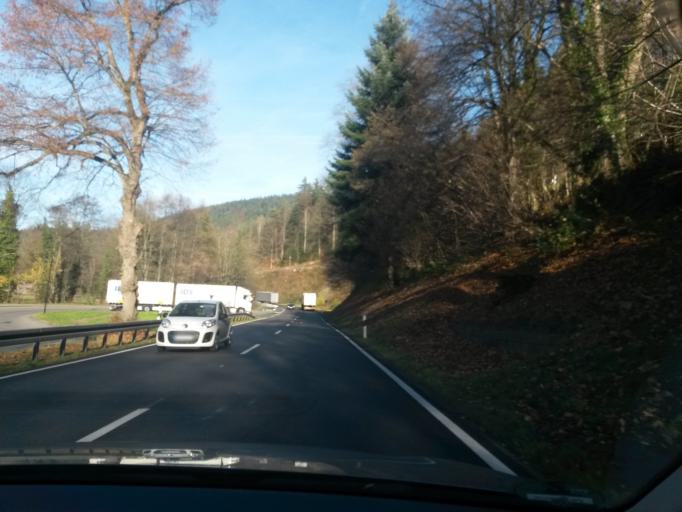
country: DE
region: Baden-Wuerttemberg
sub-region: Karlsruhe Region
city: Hofen an der Enz
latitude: 48.7955
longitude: 8.5820
